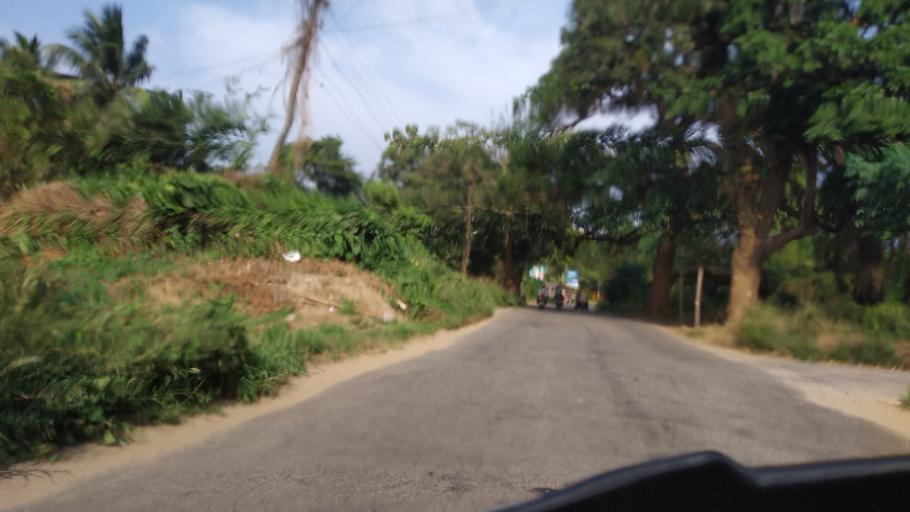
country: IN
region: Kerala
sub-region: Thrissur District
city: Chelakara
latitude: 10.5969
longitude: 76.5257
